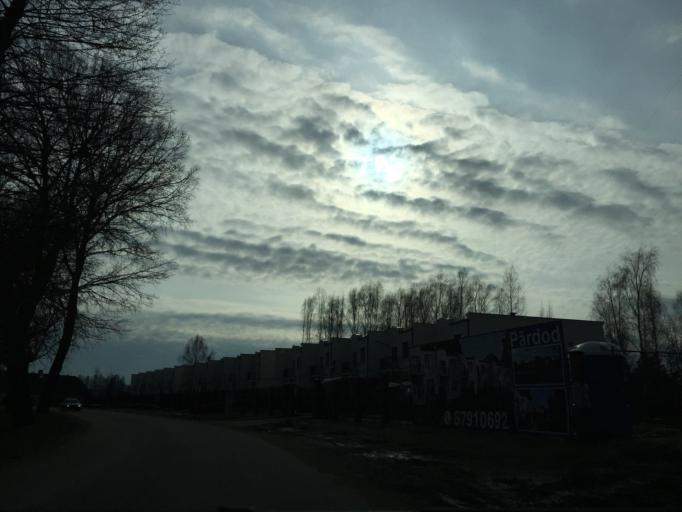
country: LV
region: Stopini
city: Ulbroka
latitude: 56.9385
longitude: 24.2858
